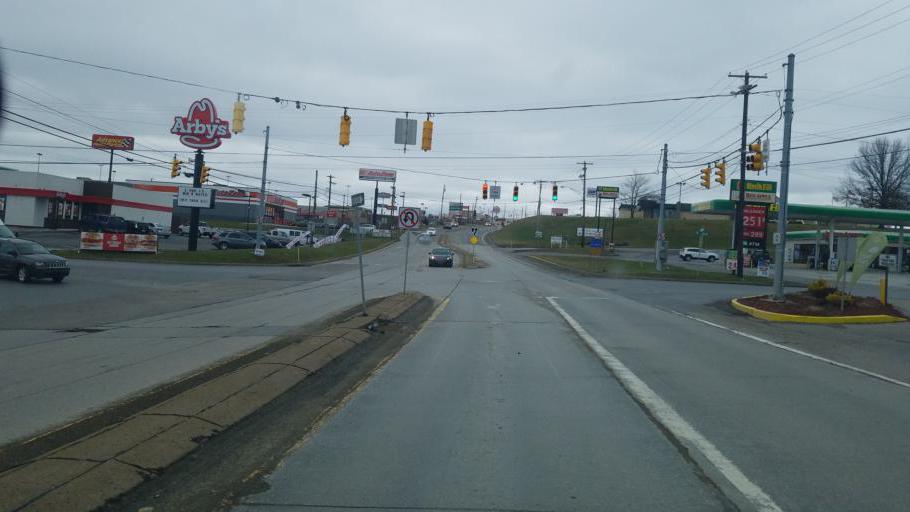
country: US
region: Pennsylvania
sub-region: Clarion County
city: Clarion
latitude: 41.1896
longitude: -79.3934
